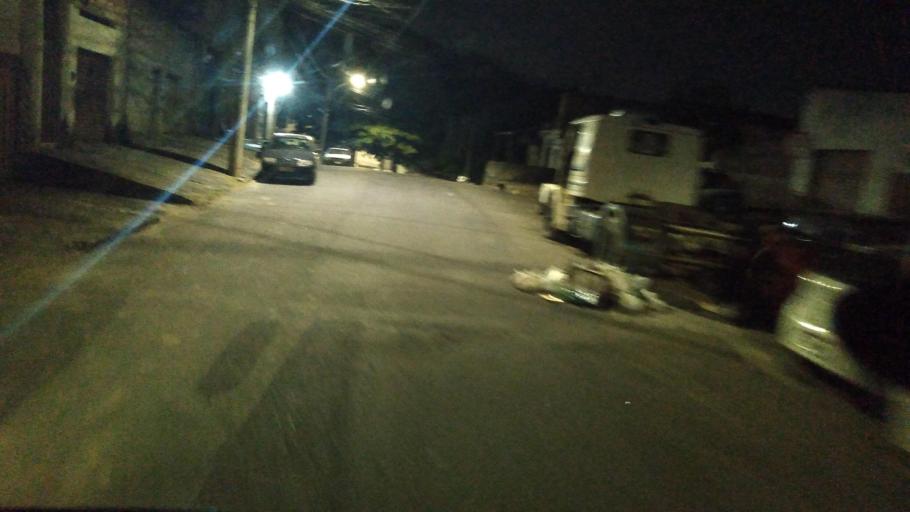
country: BR
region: Minas Gerais
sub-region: Belo Horizonte
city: Belo Horizonte
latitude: -19.8850
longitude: -43.9631
